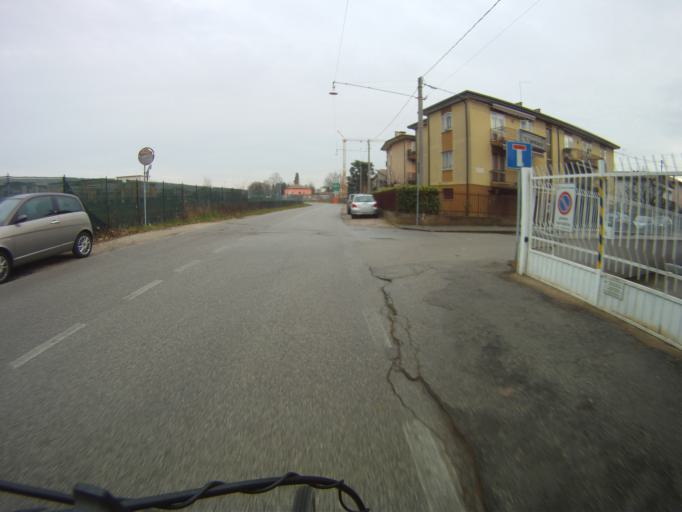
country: IT
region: Veneto
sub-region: Provincia di Padova
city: Padova
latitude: 45.3891
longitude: 11.9018
